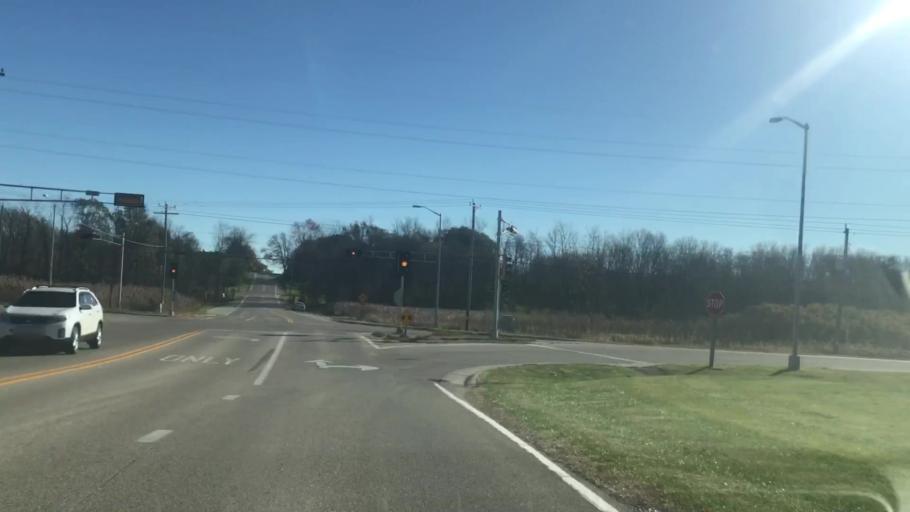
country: US
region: Wisconsin
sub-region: Waukesha County
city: Menomonee Falls
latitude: 43.1699
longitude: -88.1453
